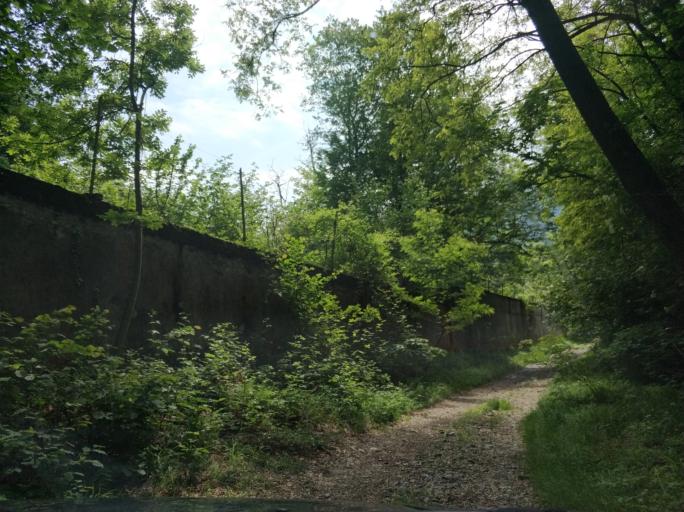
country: IT
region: Piedmont
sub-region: Provincia di Torino
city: Fiano
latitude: 45.1993
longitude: 7.5261
